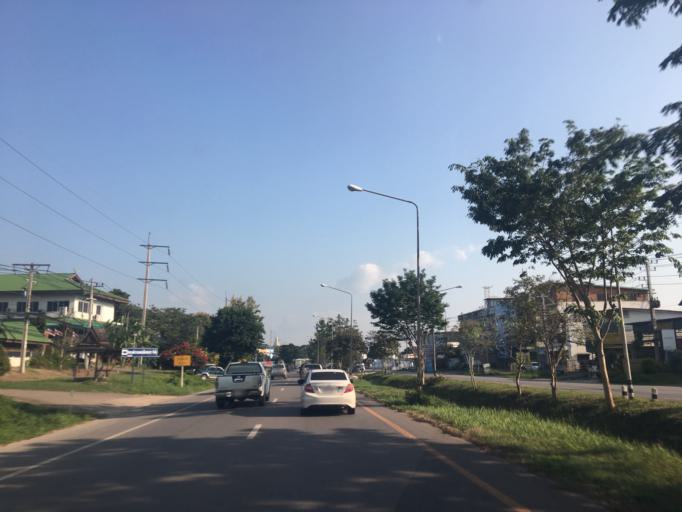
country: TH
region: Phayao
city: Phayao
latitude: 19.1672
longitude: 99.9098
